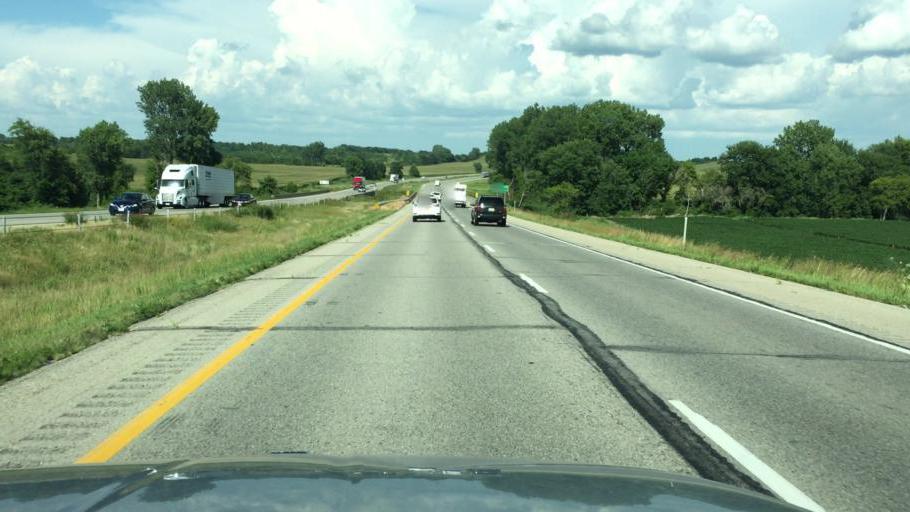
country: US
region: Iowa
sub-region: Poweshiek County
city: Grinnell
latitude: 41.6924
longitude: -92.8668
